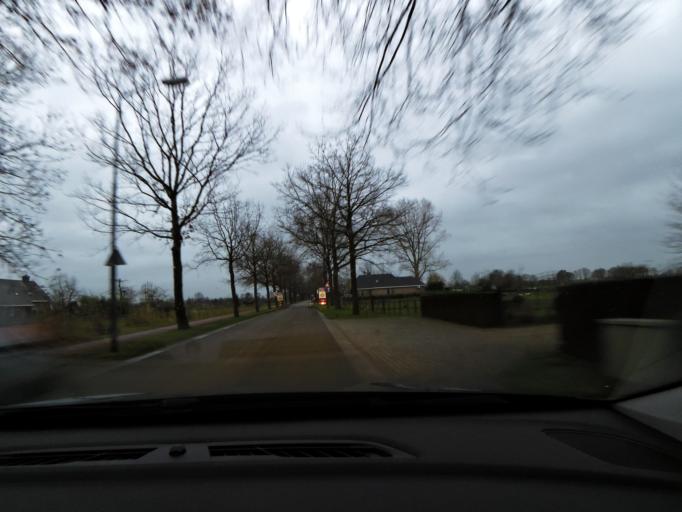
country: NL
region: North Brabant
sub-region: Gemeente Waalwijk
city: Waspik
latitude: 51.6693
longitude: 4.9835
